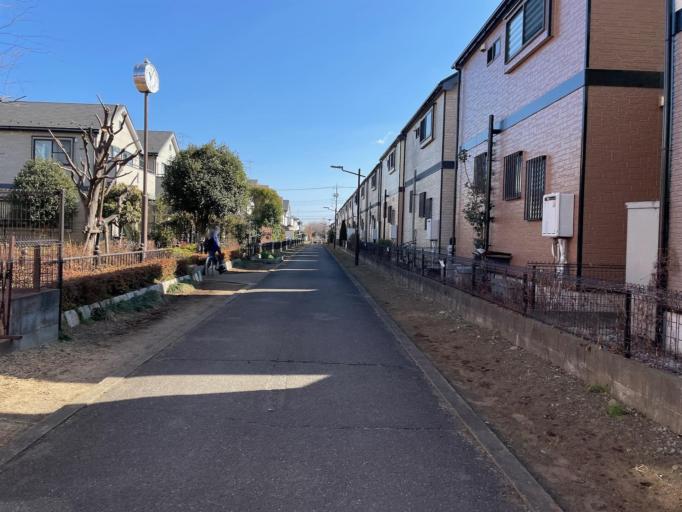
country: JP
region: Tokyo
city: Fussa
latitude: 35.7553
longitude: 139.3585
